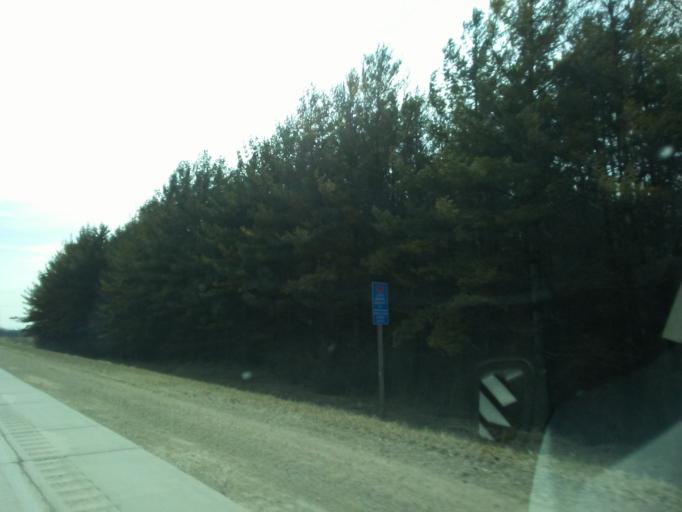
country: US
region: Iowa
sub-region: Winneshiek County
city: Decorah
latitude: 43.3363
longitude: -91.8122
